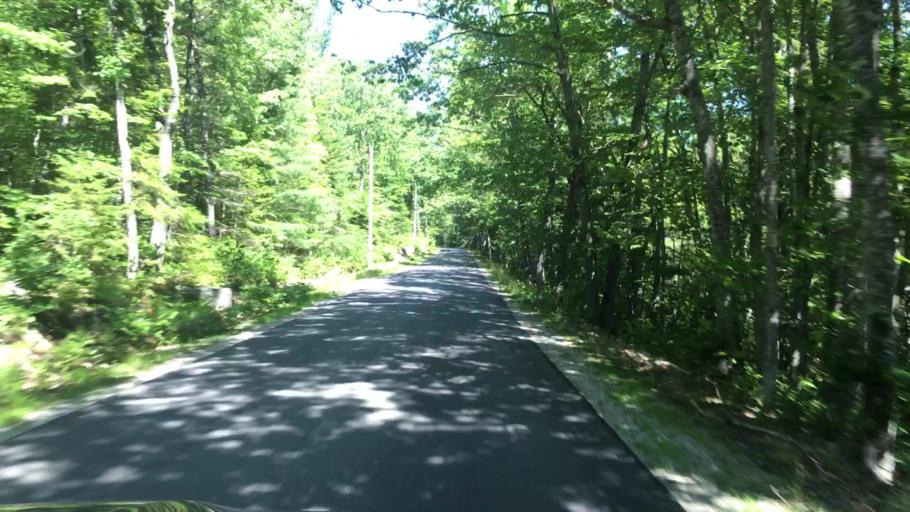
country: US
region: Maine
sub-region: Hancock County
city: Sedgwick
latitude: 44.3348
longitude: -68.6610
